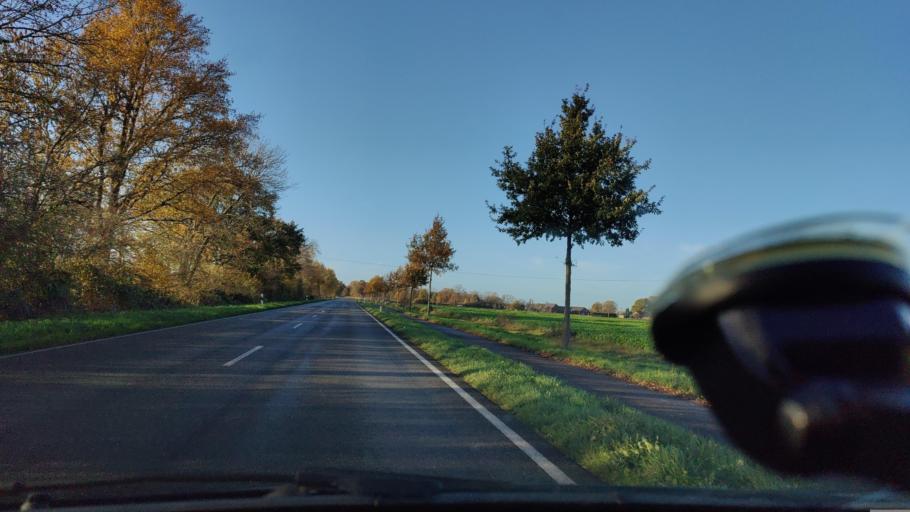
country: DE
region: North Rhine-Westphalia
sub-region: Regierungsbezirk Dusseldorf
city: Kevelaer
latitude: 51.5721
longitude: 6.2279
